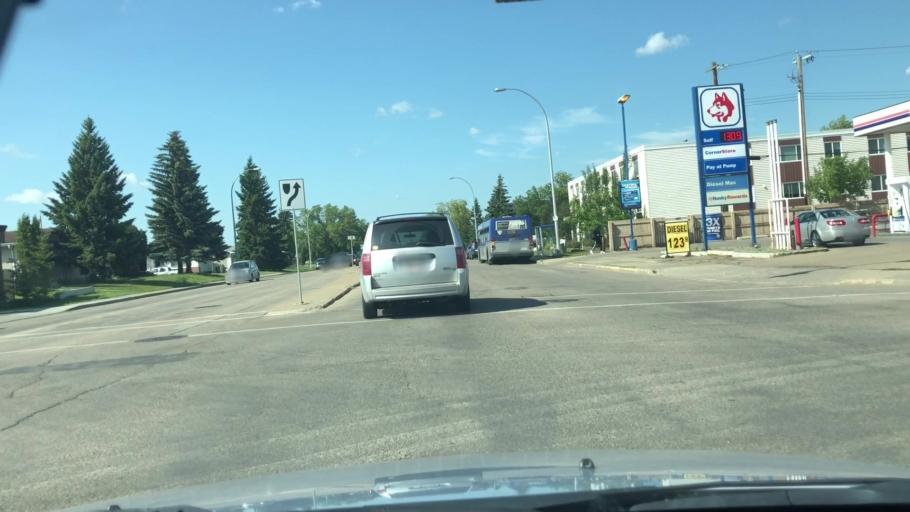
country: CA
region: Alberta
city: Edmonton
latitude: 53.5921
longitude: -113.4429
